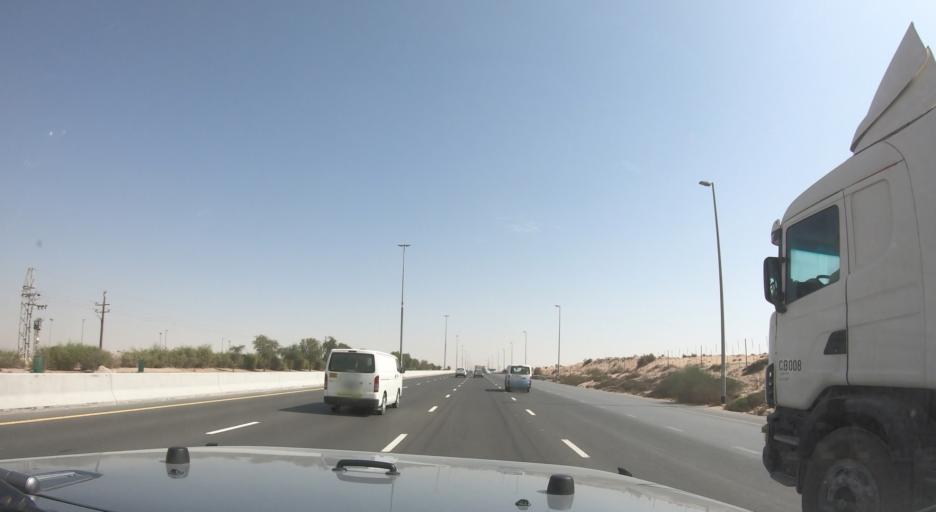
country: AE
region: Ash Shariqah
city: Sharjah
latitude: 25.1649
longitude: 55.4828
